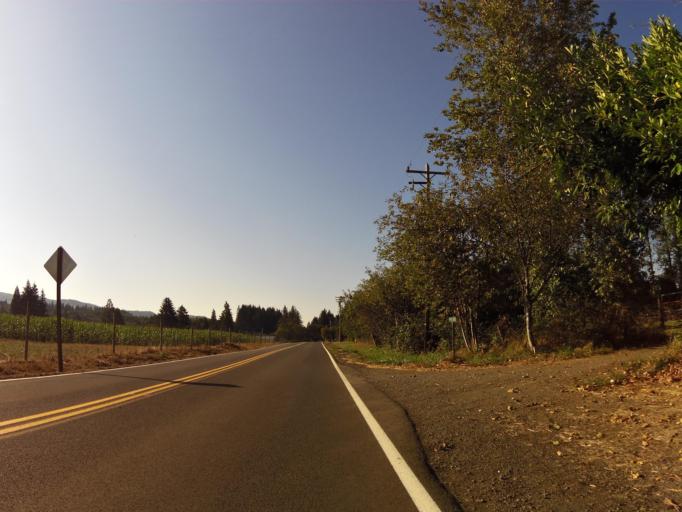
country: US
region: Oregon
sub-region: Tillamook County
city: Tillamook
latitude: 45.3896
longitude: -123.7945
